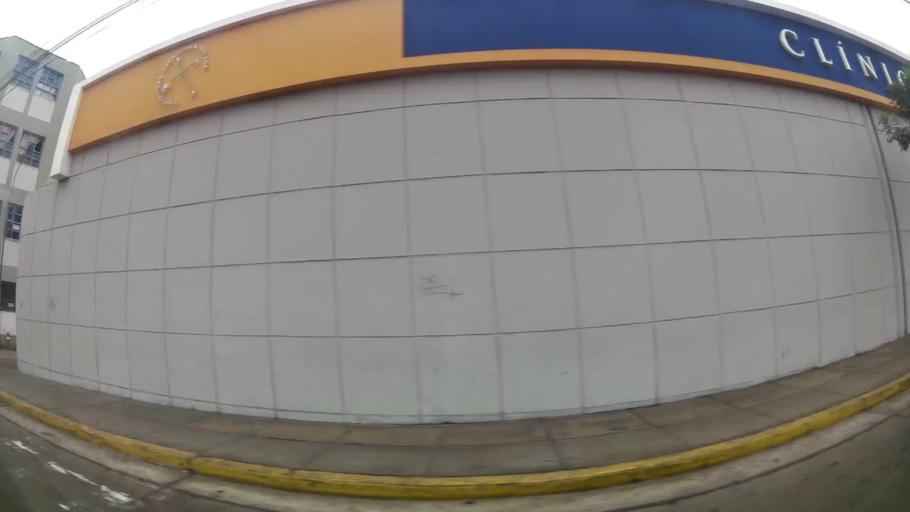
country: PE
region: Lima
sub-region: Lima
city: San Isidro
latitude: -12.1198
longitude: -77.0260
